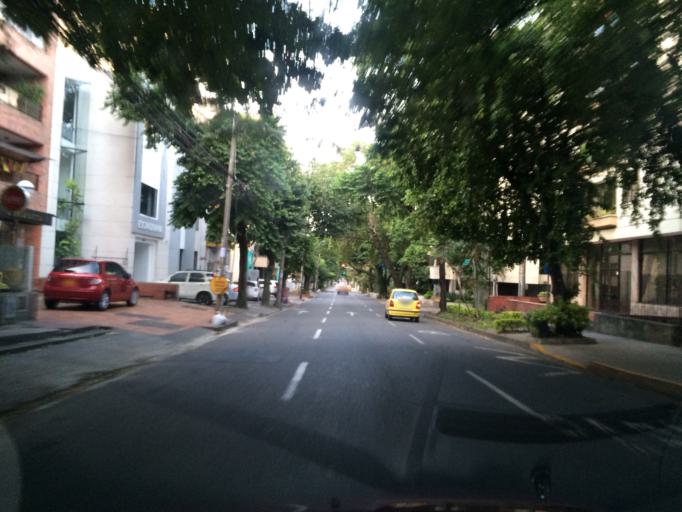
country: CO
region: Valle del Cauca
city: Cali
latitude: 3.4519
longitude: -76.5394
